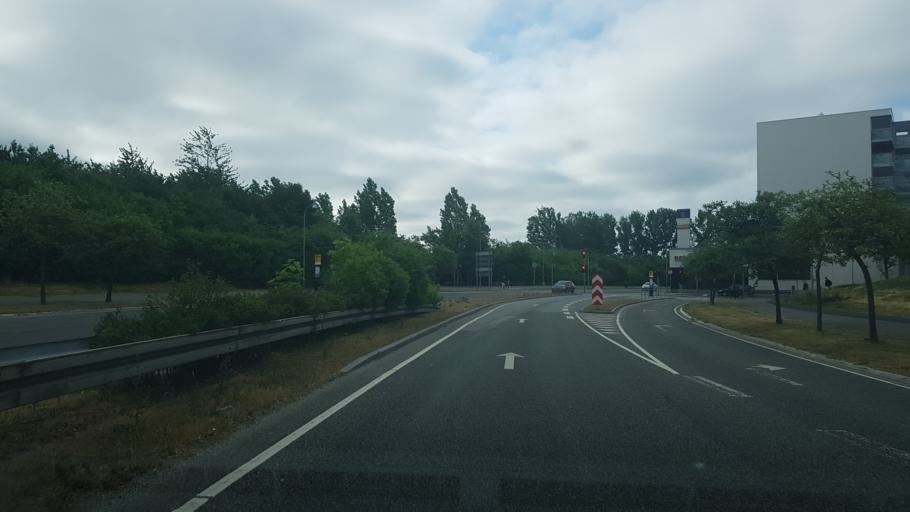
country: DK
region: Capital Region
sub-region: Vallensbaek Kommune
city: Vallensbaek
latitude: 55.6254
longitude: 12.3887
